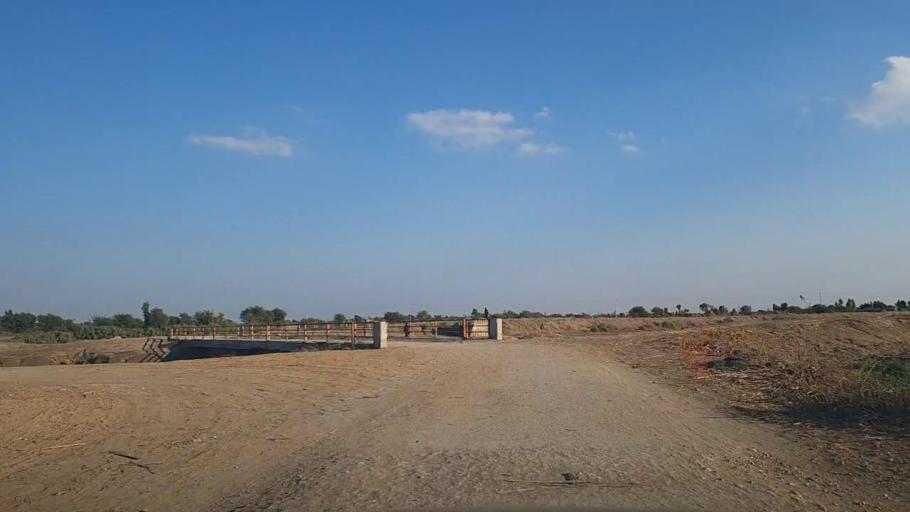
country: PK
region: Sindh
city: Jhol
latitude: 25.9261
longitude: 69.0153
